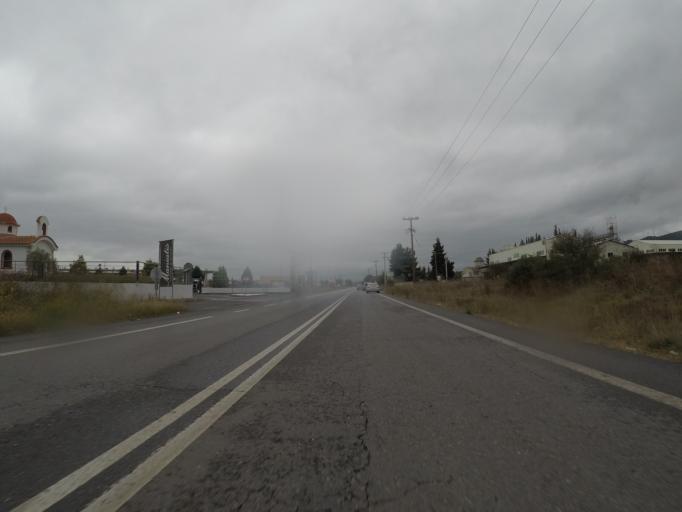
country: GR
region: Peloponnese
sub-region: Nomos Arkadias
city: Tripoli
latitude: 37.5403
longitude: 22.3908
